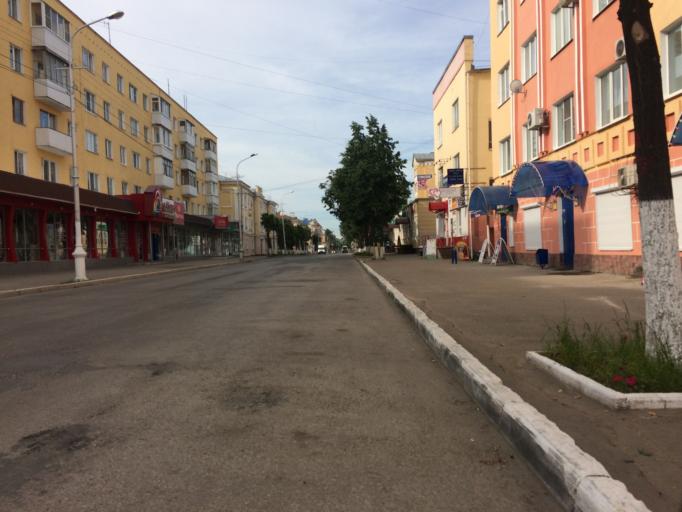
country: RU
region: Mariy-El
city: Yoshkar-Ola
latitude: 56.6370
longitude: 47.8988
